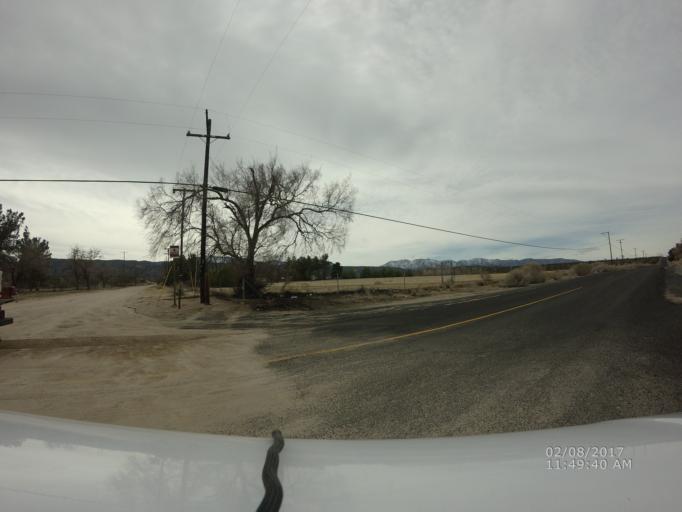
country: US
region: California
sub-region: San Bernardino County
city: Pinon Hills
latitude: 34.4695
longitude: -117.7481
